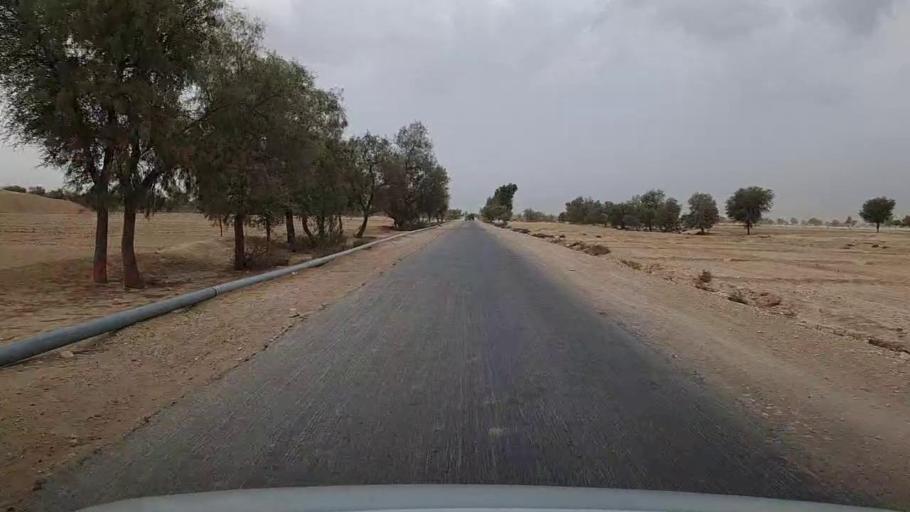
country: PK
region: Sindh
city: Sehwan
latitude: 26.3282
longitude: 67.7252
